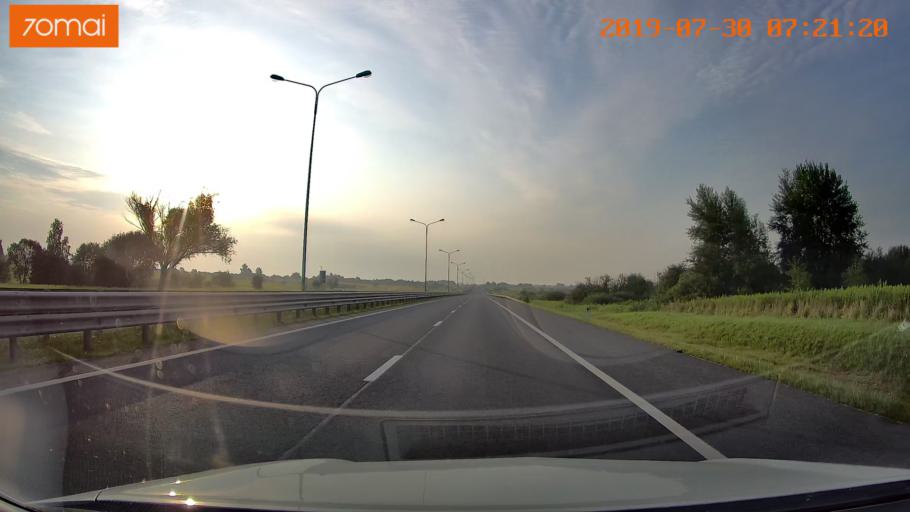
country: RU
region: Kaliningrad
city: Bol'shoe Isakovo
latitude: 54.6968
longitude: 20.7262
